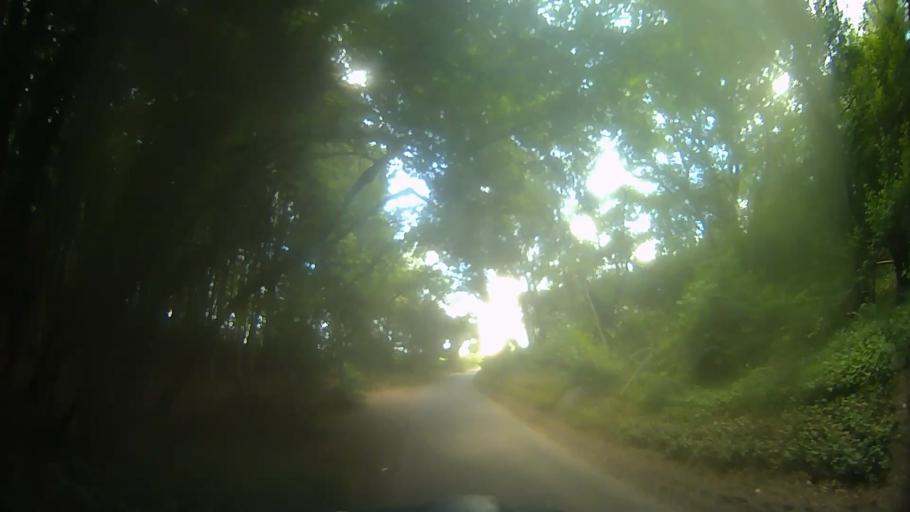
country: GB
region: England
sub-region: Hampshire
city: Andover
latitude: 51.2473
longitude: -1.4415
